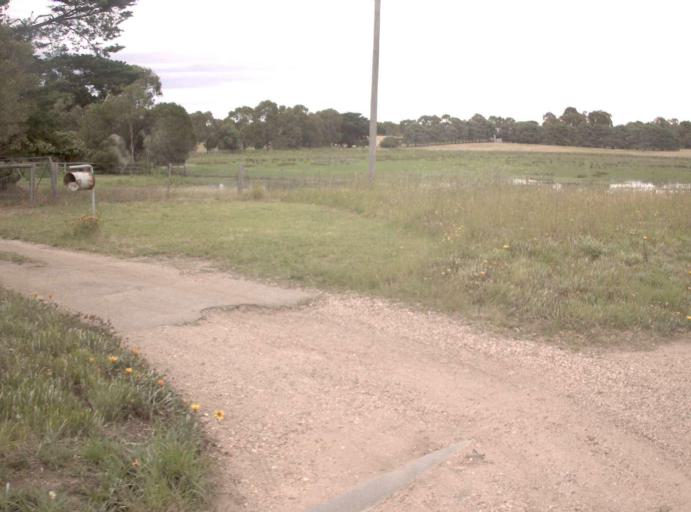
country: AU
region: Victoria
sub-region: East Gippsland
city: Bairnsdale
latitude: -37.8258
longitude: 147.5116
